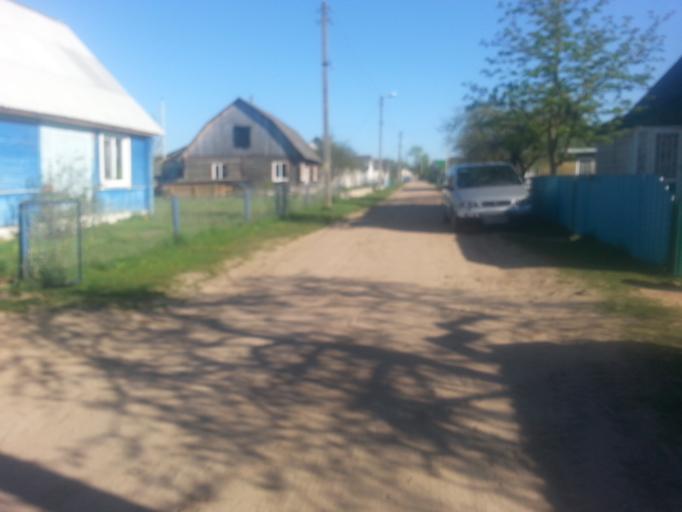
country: BY
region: Minsk
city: Narach
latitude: 54.9315
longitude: 26.6812
